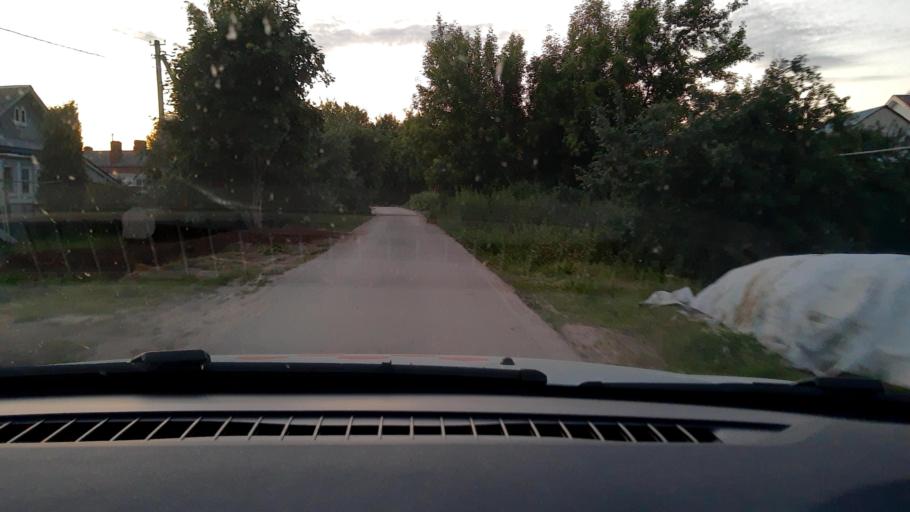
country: RU
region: Nizjnij Novgorod
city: Afonino
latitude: 56.2337
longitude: 44.1052
